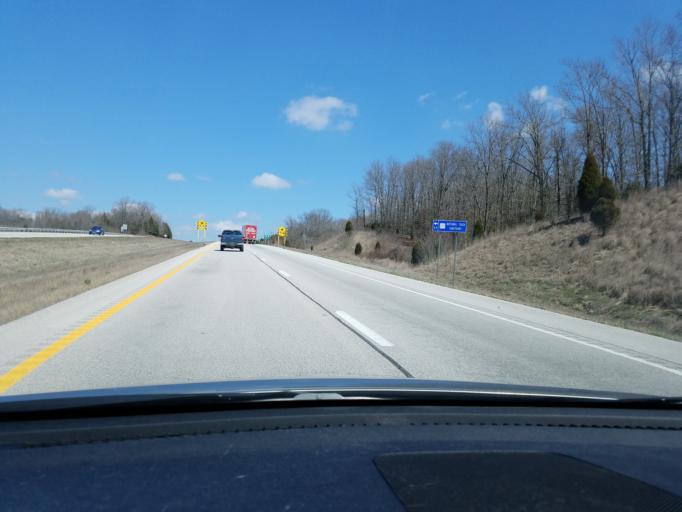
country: US
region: Missouri
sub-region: Taney County
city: Merriam Woods
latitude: 36.8390
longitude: -93.2187
